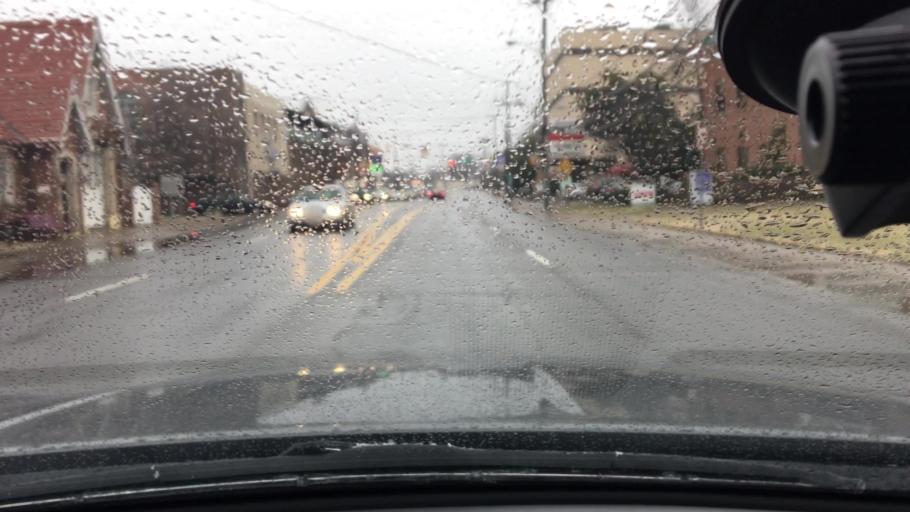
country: US
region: Tennessee
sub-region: Davidson County
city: Nashville
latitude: 36.1294
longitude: -86.8025
